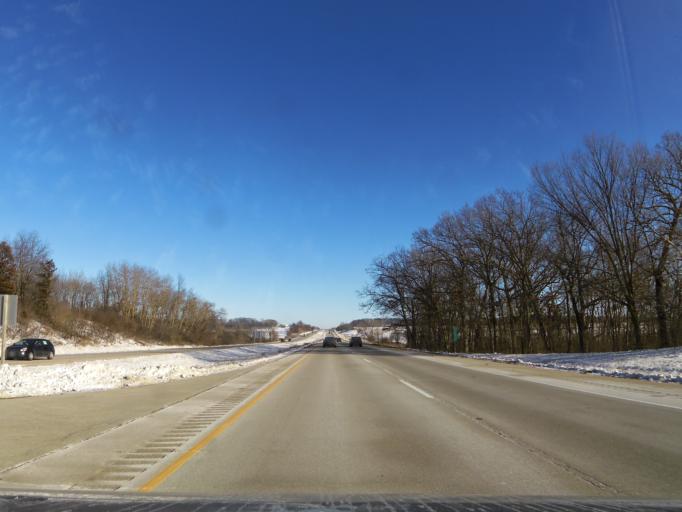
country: US
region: Wisconsin
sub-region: Dane County
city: Deerfield
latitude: 43.1091
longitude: -89.0742
